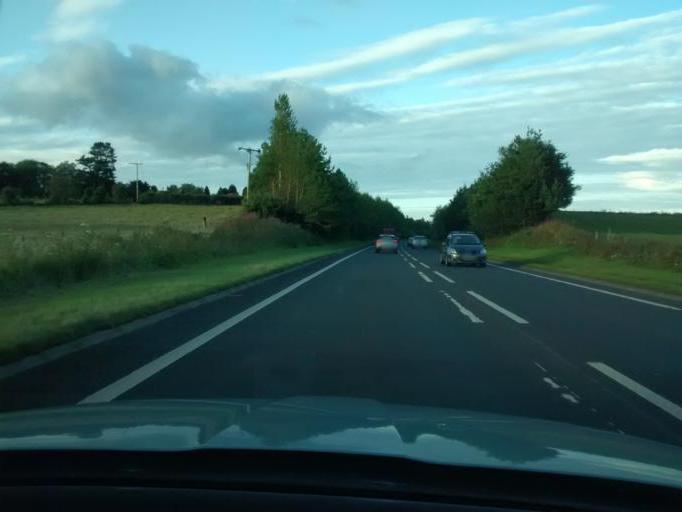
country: GB
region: Scotland
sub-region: Renfrewshire
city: Kilbarchan
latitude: 55.8248
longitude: -4.5411
